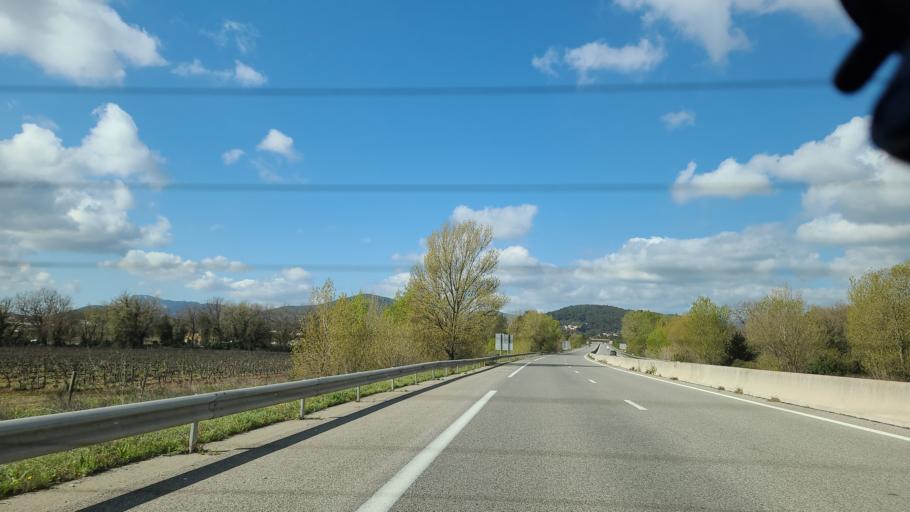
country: FR
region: Provence-Alpes-Cote d'Azur
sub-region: Departement du Var
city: Puget-Ville
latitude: 43.2542
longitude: 6.1142
